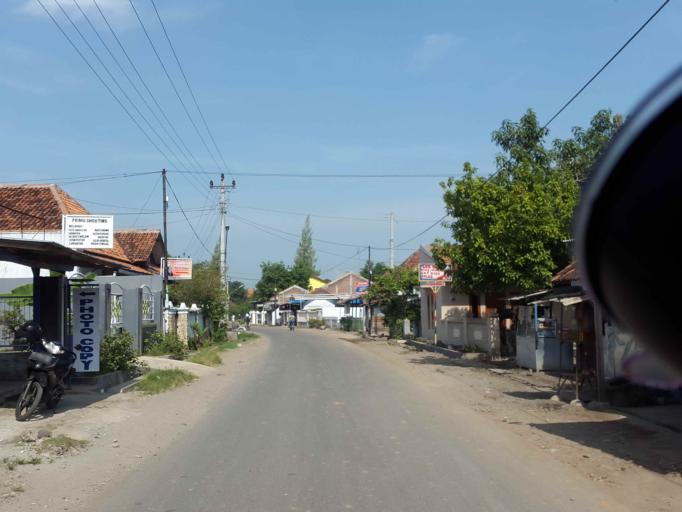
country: ID
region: Central Java
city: Pemalang
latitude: -6.9165
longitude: 109.3828
